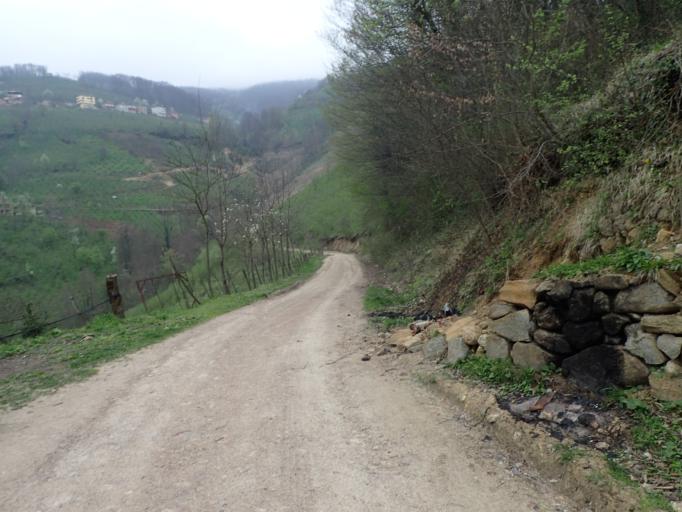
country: TR
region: Ordu
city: Korgan
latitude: 40.7753
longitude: 37.3464
